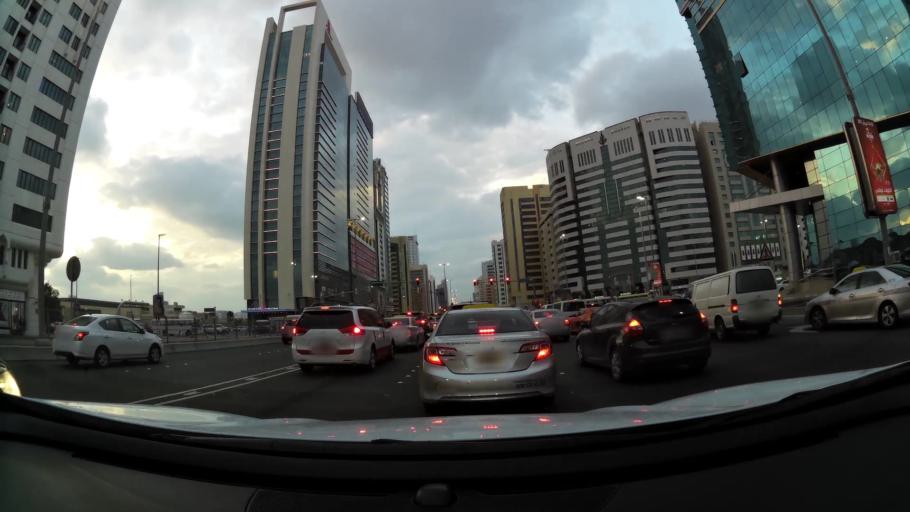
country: AE
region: Abu Dhabi
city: Abu Dhabi
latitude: 24.4698
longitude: 54.3713
